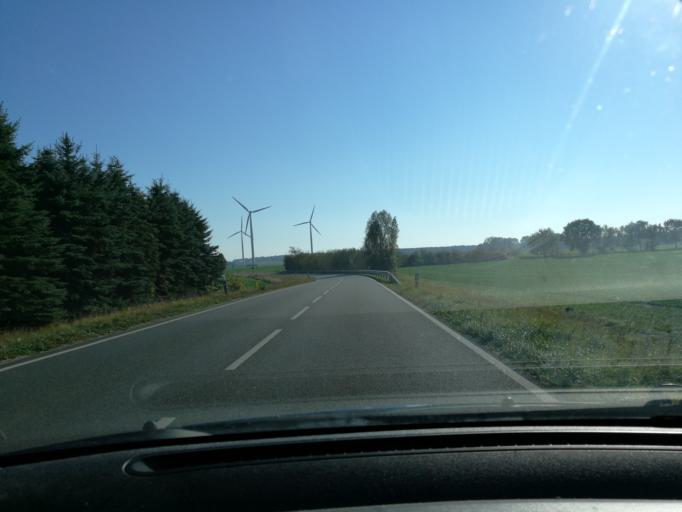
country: DE
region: Lower Saxony
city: Barendorf
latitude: 53.2240
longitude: 10.5161
